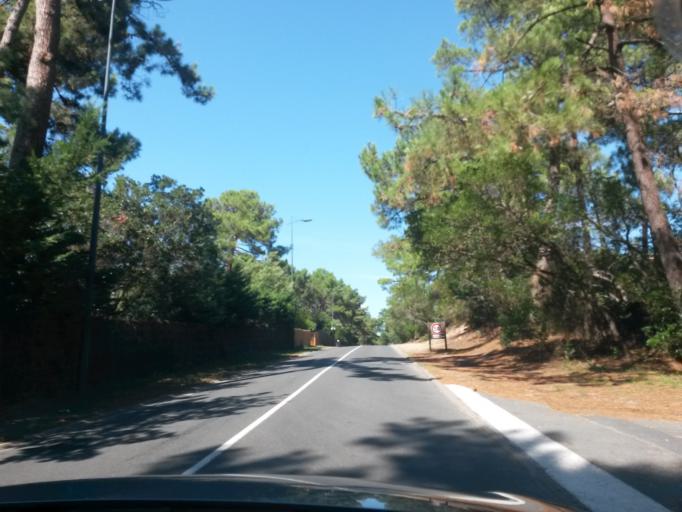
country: FR
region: Aquitaine
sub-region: Departement de la Gironde
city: Arcachon
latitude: 44.6611
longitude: -1.2437
